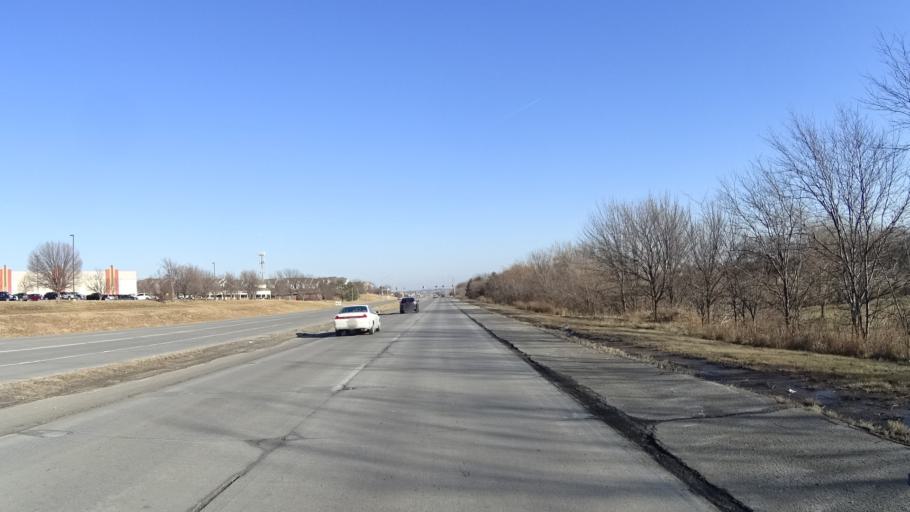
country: US
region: Nebraska
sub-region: Douglas County
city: Bennington
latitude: 41.2920
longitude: -96.1375
